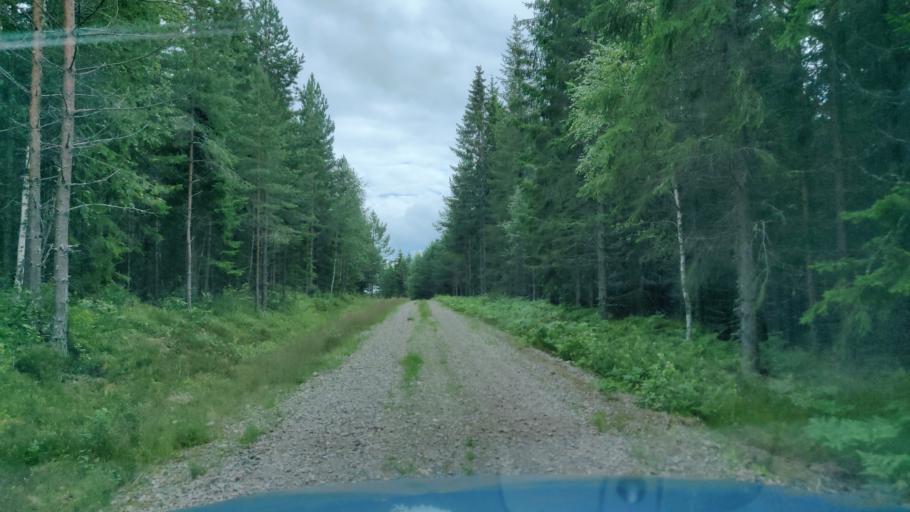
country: SE
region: Vaermland
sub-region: Hagfors Kommun
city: Hagfors
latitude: 59.9669
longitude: 13.5839
